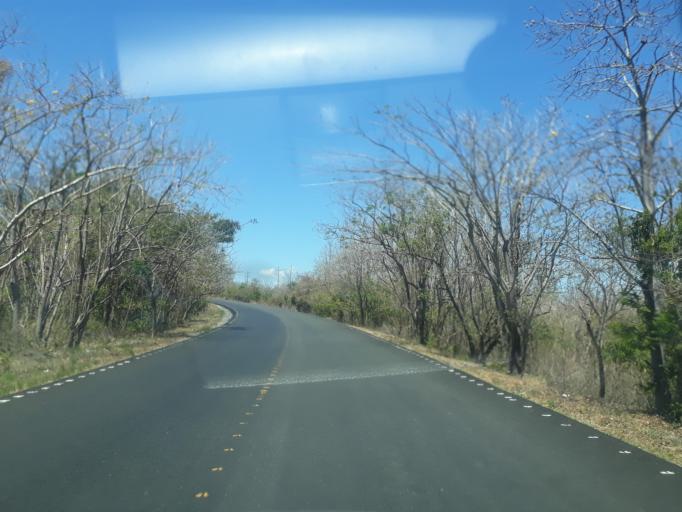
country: CR
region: Guanacaste
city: La Cruz
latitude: 10.9168
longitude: -85.6031
